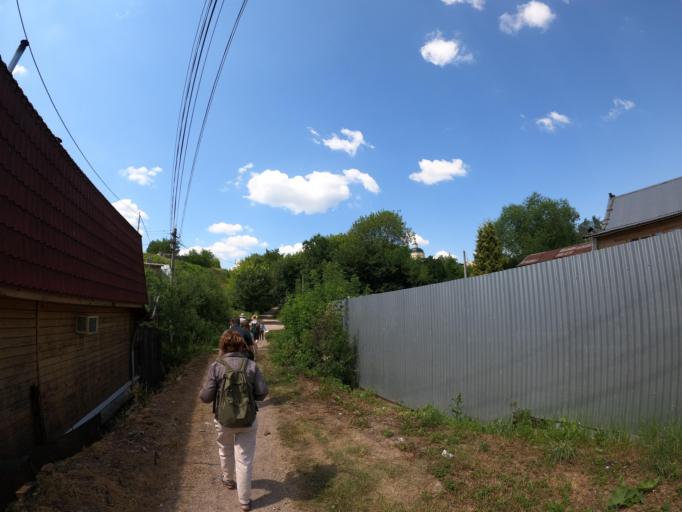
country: RU
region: Moskovskaya
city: Serpukhov
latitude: 54.9164
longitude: 37.4074
